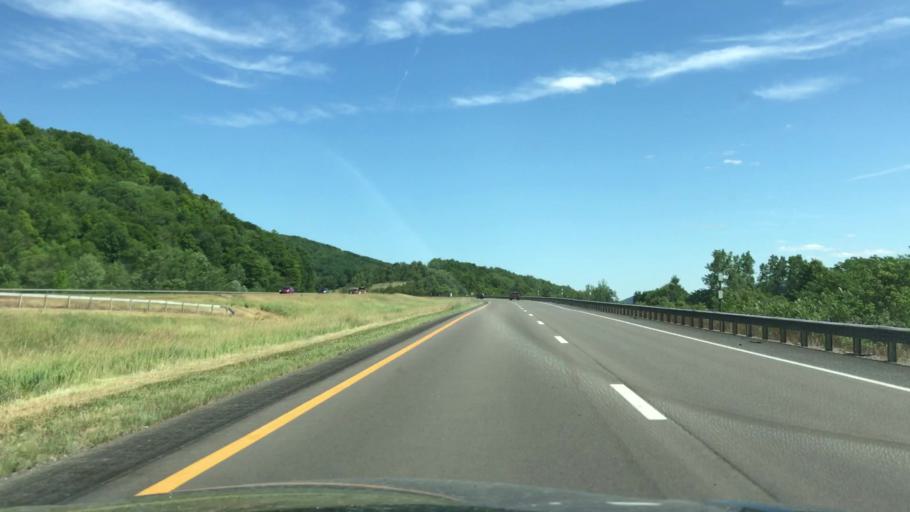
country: US
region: New York
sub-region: Steuben County
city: Bath
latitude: 42.4198
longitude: -77.4254
